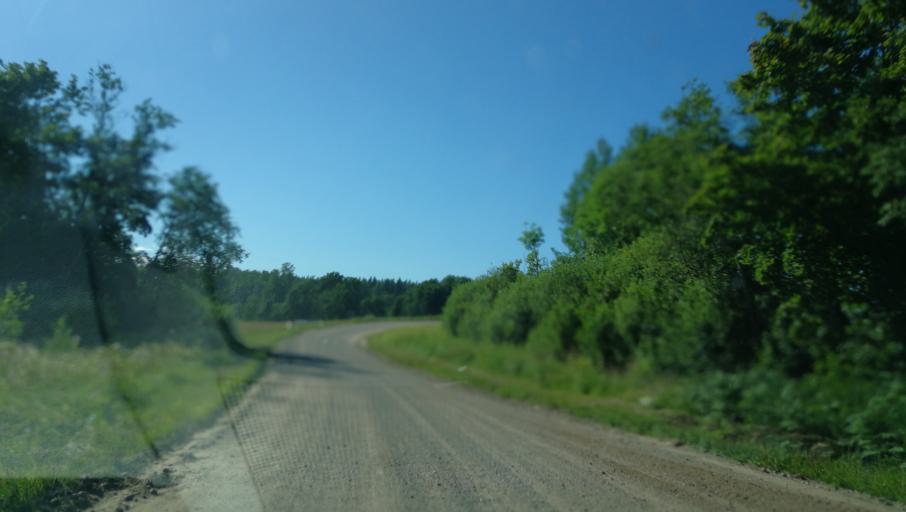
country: LV
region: Jaunpiebalga
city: Jaunpiebalga
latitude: 57.0248
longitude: 26.0291
